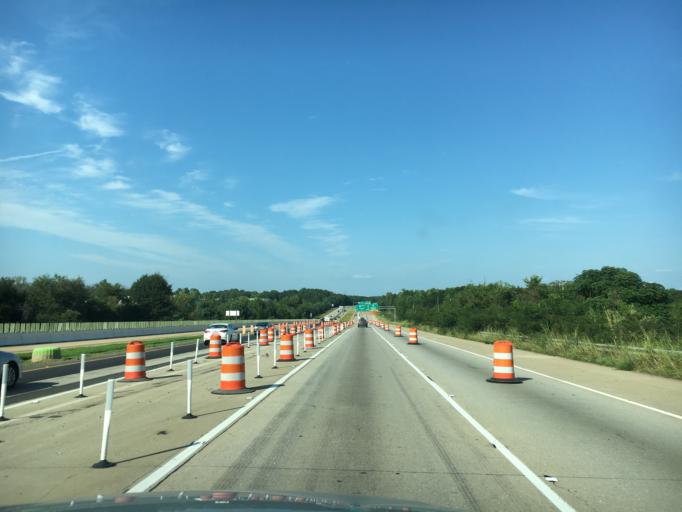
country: US
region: South Carolina
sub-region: Spartanburg County
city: Fairforest
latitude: 34.9688
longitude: -82.0270
